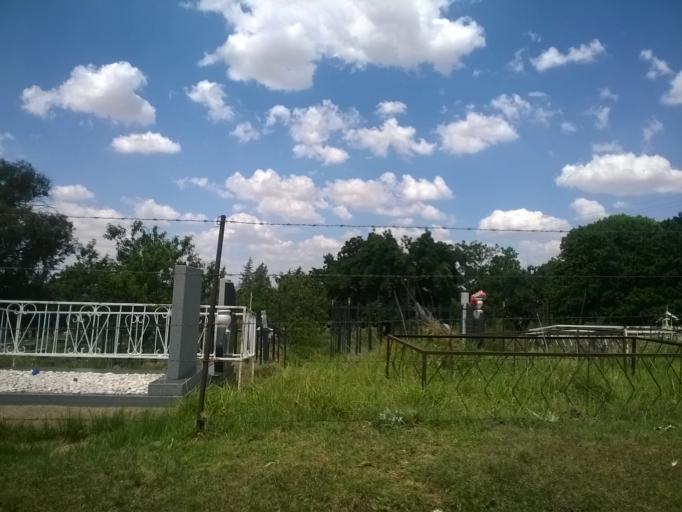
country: LS
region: Berea
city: Teyateyaneng
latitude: -29.1481
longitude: 27.7555
